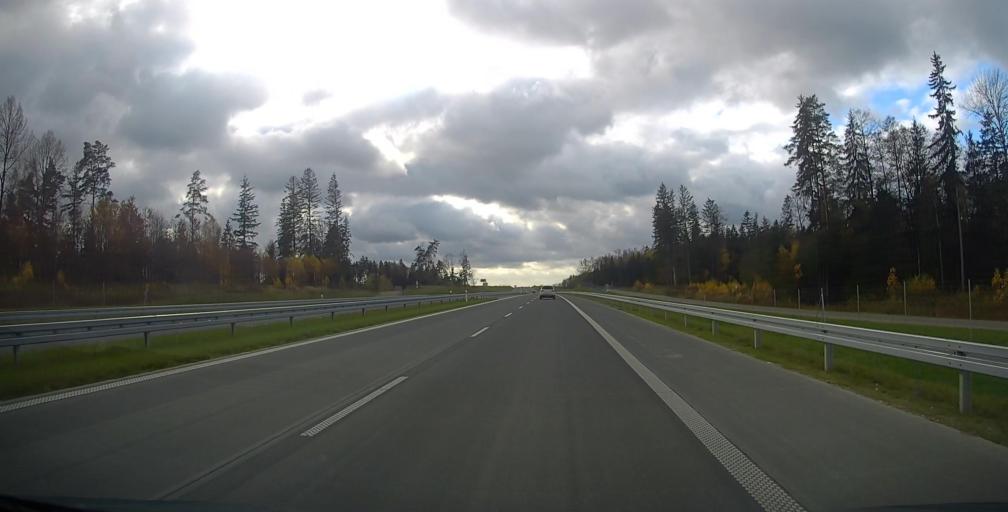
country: PL
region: Podlasie
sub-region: Powiat suwalski
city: Raczki
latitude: 53.8983
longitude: 22.6902
